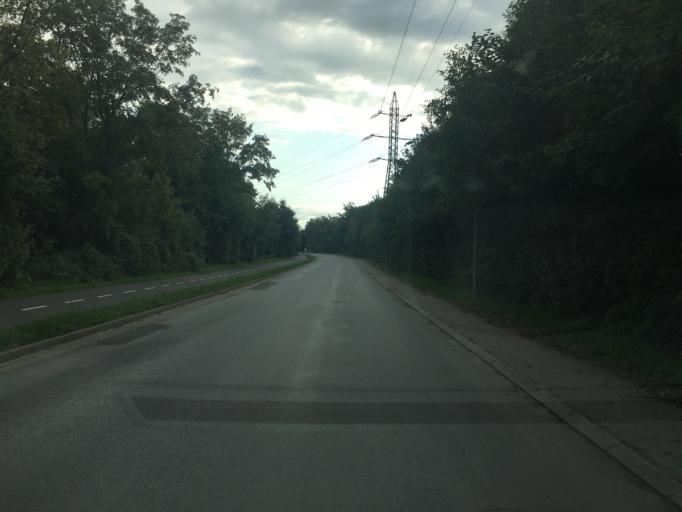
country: DK
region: South Denmark
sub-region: Tonder Kommune
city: Tonder
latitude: 54.9356
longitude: 8.8813
